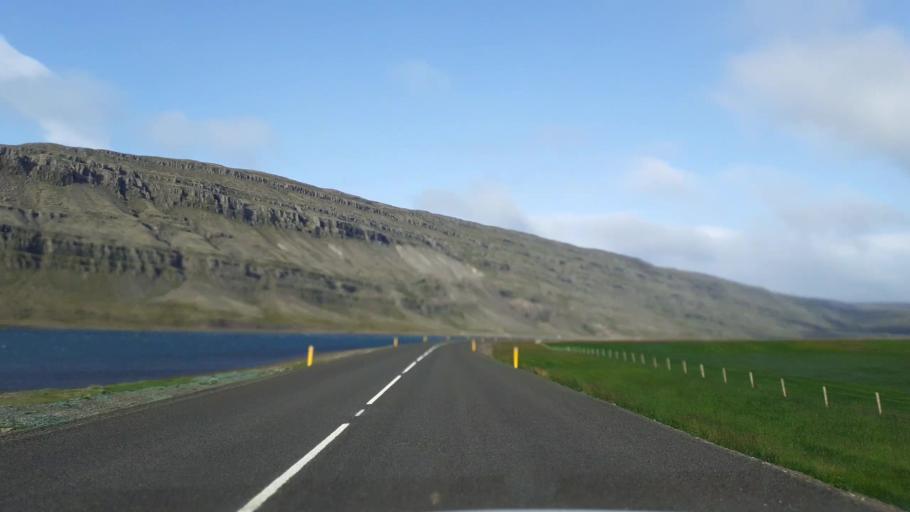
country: IS
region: East
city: Reydarfjoerdur
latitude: 64.7887
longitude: -14.4588
